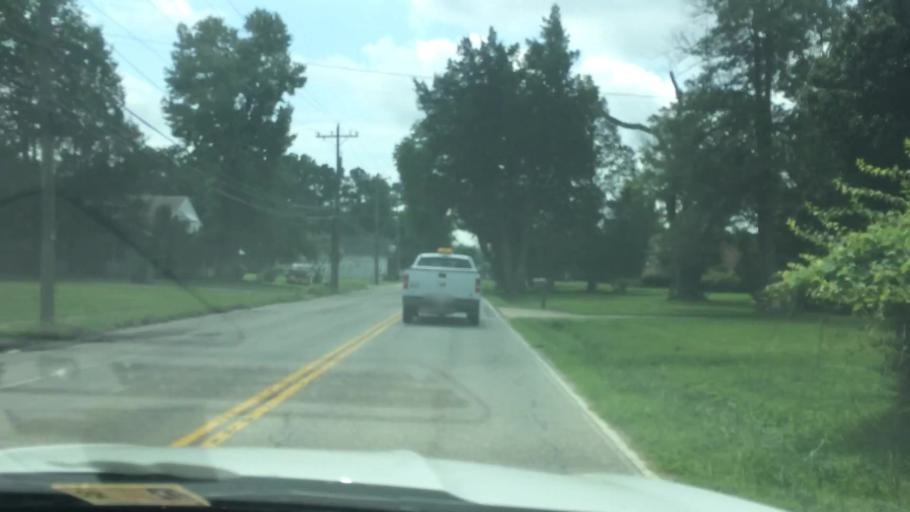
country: US
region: Virginia
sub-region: York County
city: Yorktown
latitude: 37.1957
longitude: -76.5716
